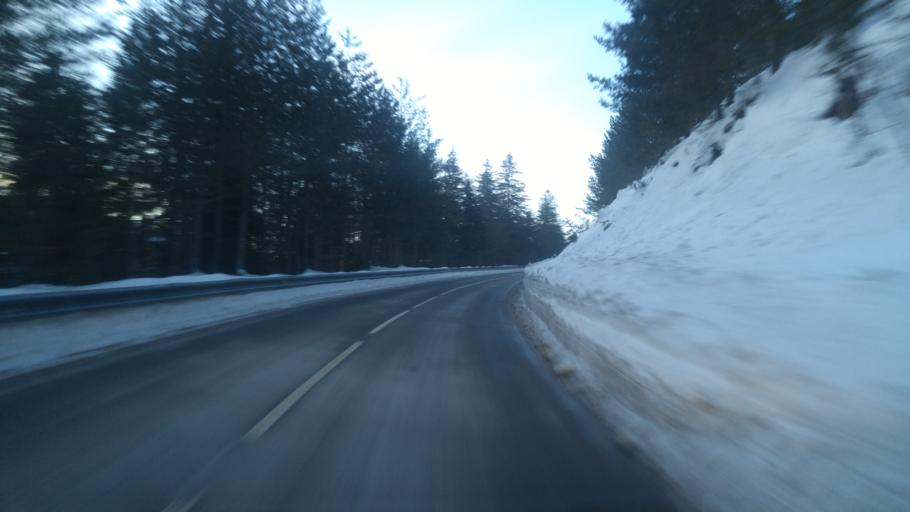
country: AT
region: Lower Austria
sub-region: Politischer Bezirk Wiener Neustadt
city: Rohr im Gebirge
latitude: 47.8678
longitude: 15.7951
